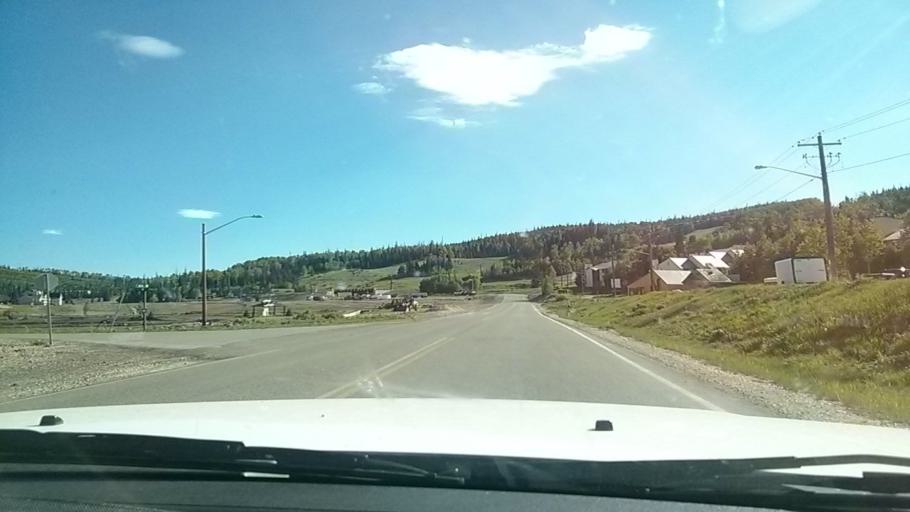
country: US
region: Utah
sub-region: Iron County
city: Parowan
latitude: 37.6925
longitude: -112.8500
